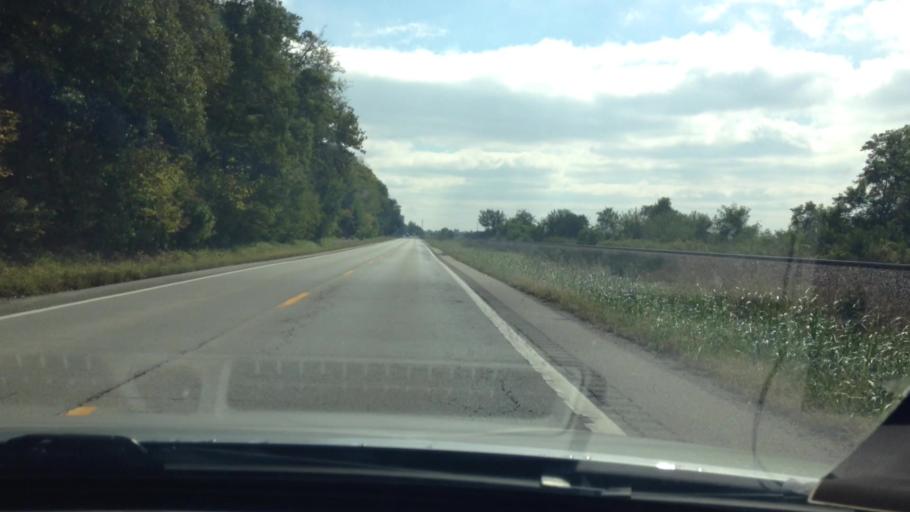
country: US
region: Kansas
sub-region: Leavenworth County
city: Lansing
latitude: 39.2899
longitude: -94.8403
